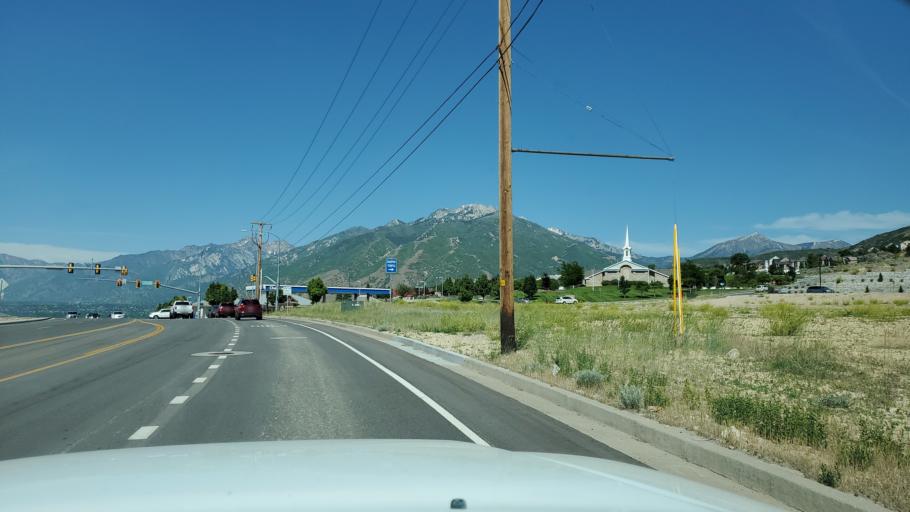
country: US
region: Utah
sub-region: Salt Lake County
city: Draper
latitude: 40.4845
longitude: -111.8852
